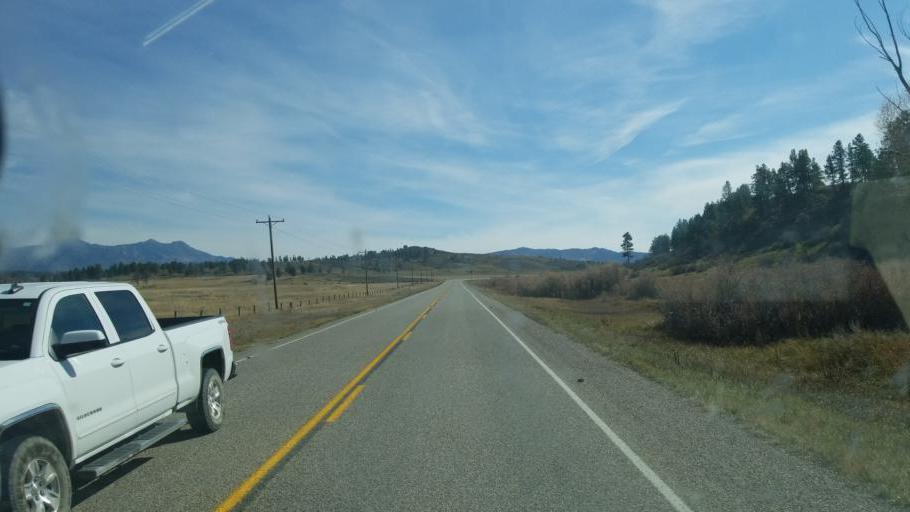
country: US
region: New Mexico
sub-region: Rio Arriba County
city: Dulce
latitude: 37.0347
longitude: -106.8370
